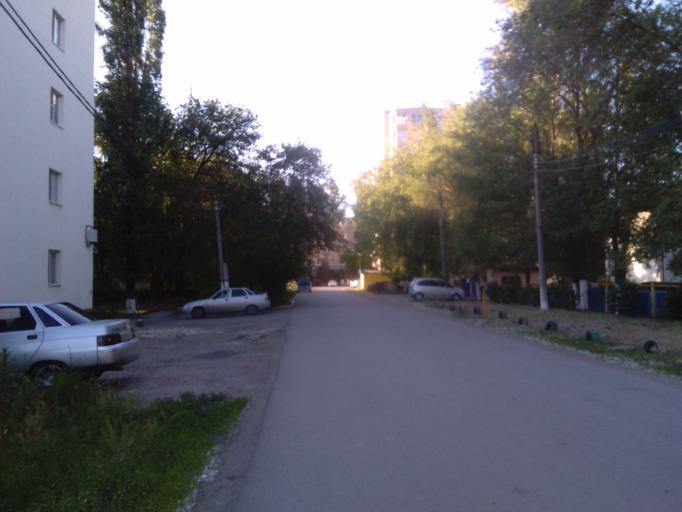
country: RU
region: Rostov
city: Bataysk
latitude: 47.1249
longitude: 39.7341
